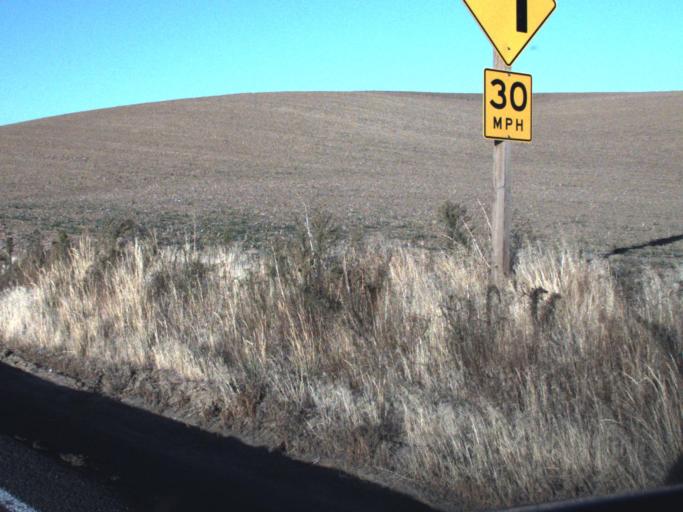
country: US
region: Washington
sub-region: Adams County
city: Ritzville
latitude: 46.6794
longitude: -118.3792
